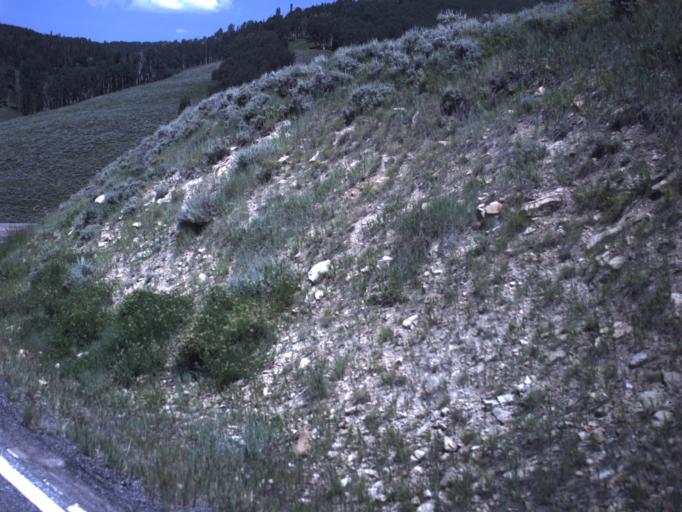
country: US
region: Utah
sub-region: Sanpete County
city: Fairview
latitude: 39.6852
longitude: -111.2446
